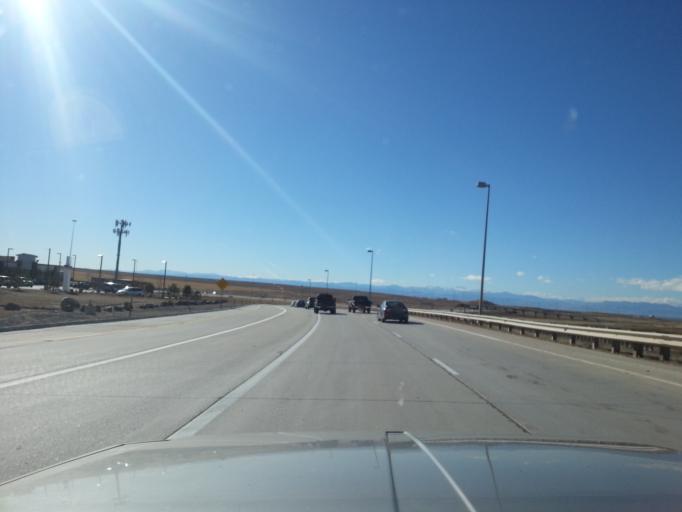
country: US
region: Colorado
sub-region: Adams County
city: Aurora
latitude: 39.8376
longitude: -104.7196
